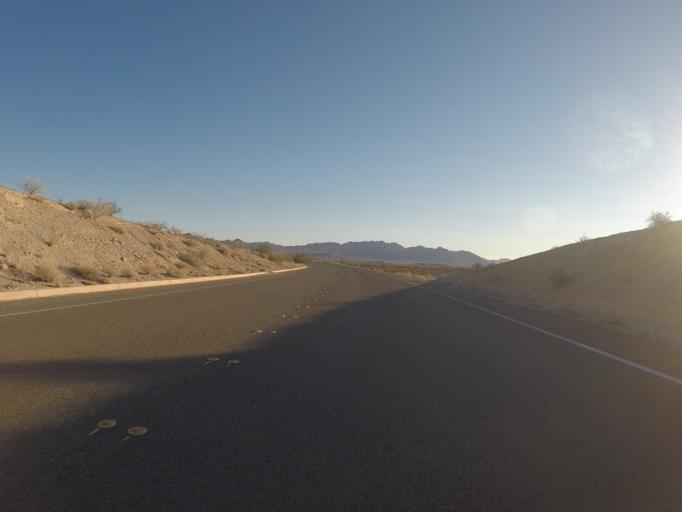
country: US
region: Nevada
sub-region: Clark County
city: Moapa Valley
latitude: 36.3223
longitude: -114.4931
